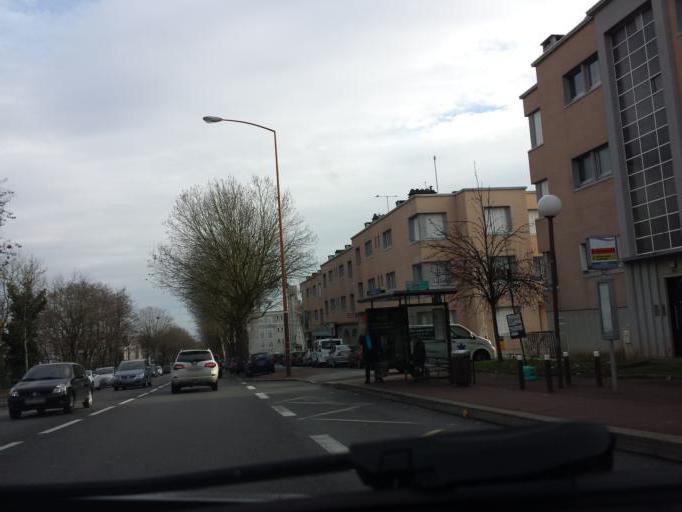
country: FR
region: Ile-de-France
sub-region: Departement des Hauts-de-Seine
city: Chatenay-Malabry
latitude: 48.7647
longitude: 2.2657
